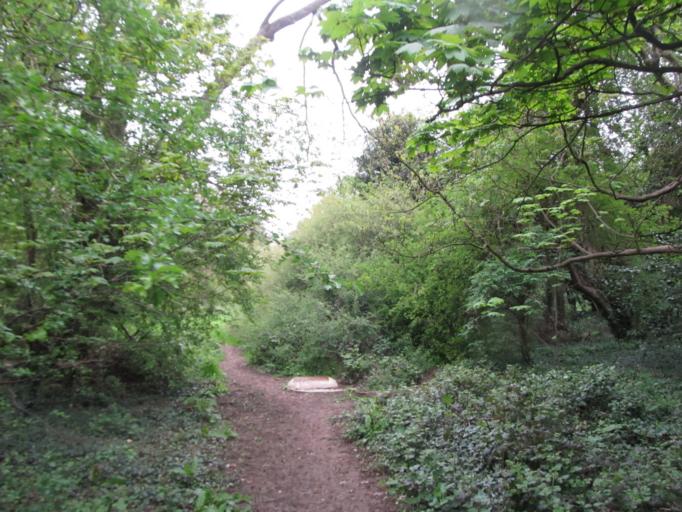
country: GB
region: England
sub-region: Royal Borough of Windsor and Maidenhead
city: Bisham
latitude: 51.5373
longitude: -0.7601
